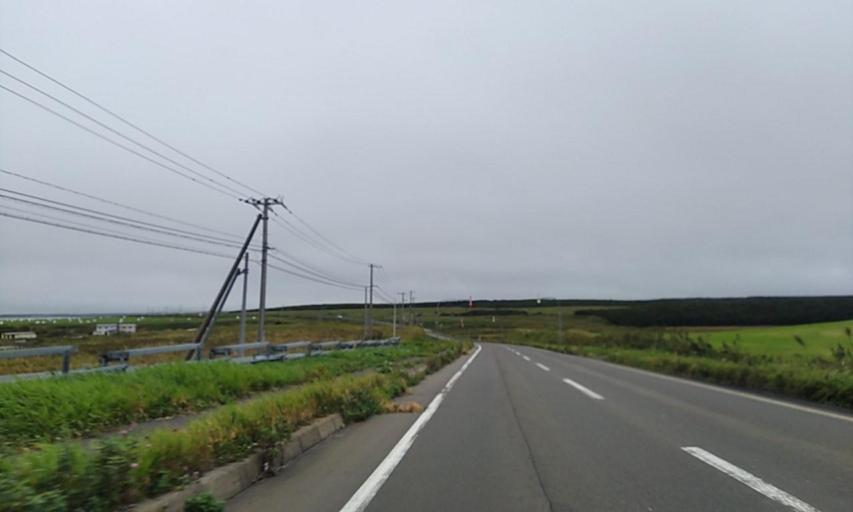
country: JP
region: Hokkaido
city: Nemuro
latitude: 43.3869
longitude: 145.6696
